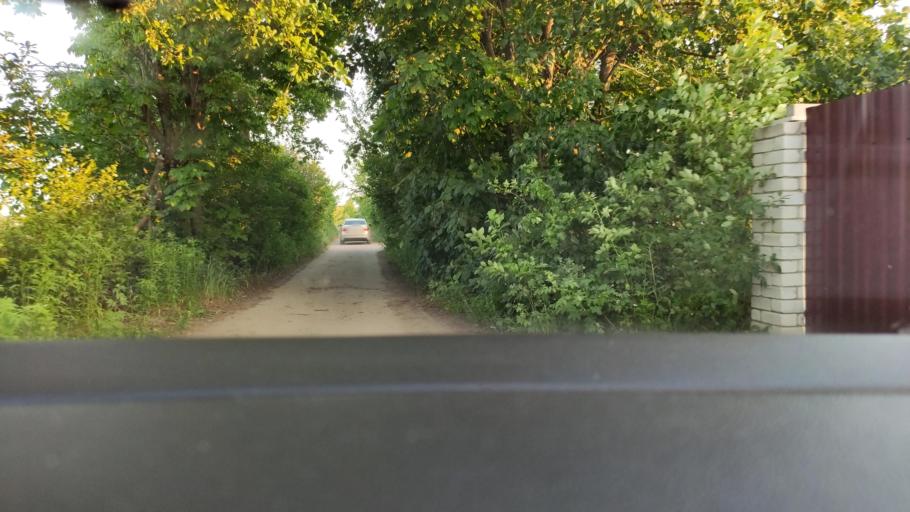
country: RU
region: Voronezj
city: Ramon'
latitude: 51.9117
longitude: 39.1769
